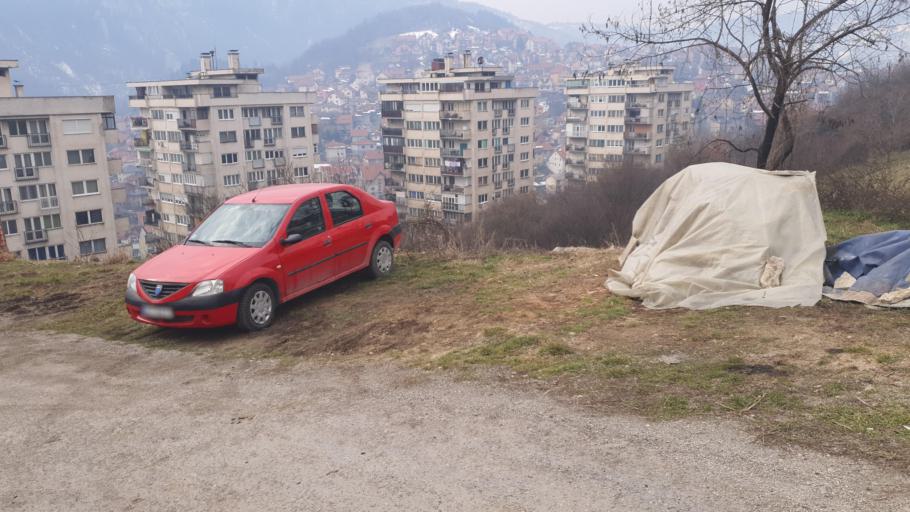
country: RS
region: Central Serbia
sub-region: Zlatiborski Okrug
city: Uzice
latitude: 43.8591
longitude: 19.8345
